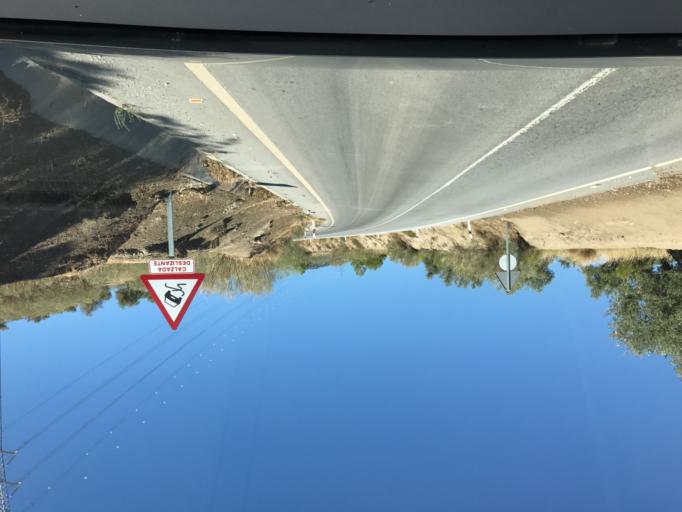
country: ES
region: Andalusia
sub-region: Provincia de Granada
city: Jun
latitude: 37.2100
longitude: -3.5710
